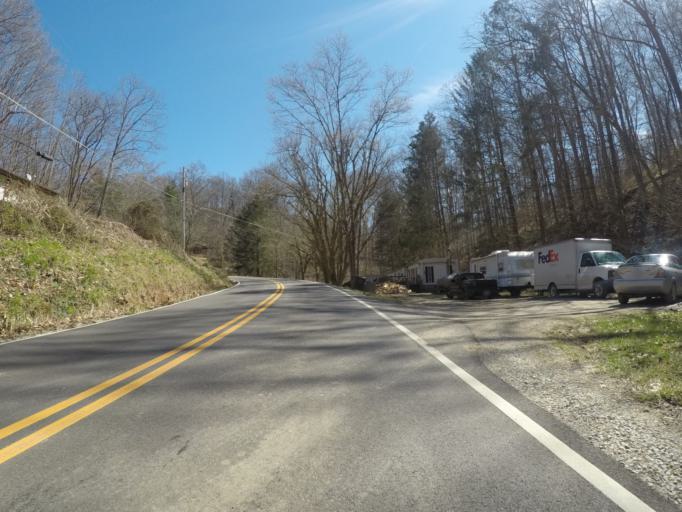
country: US
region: Ohio
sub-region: Lawrence County
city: South Point
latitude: 38.4606
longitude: -82.5555
